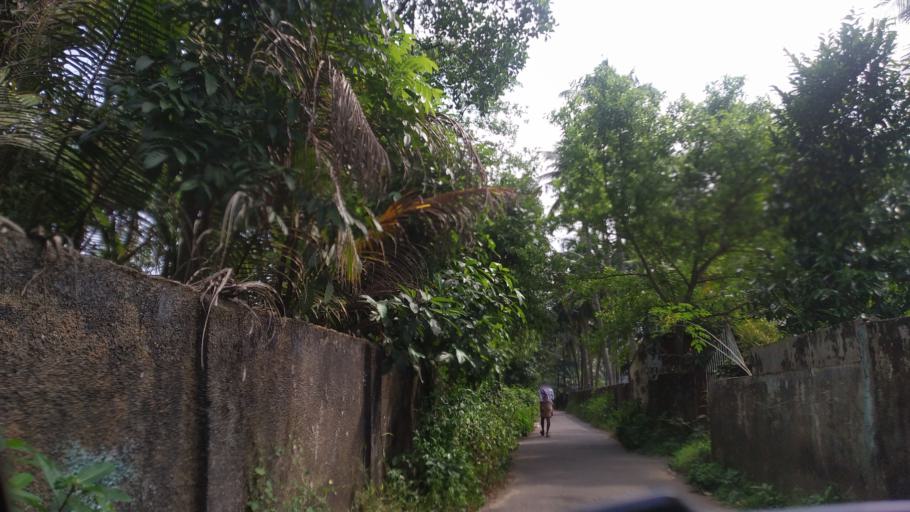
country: IN
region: Kerala
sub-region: Ernakulam
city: Elur
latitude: 10.0888
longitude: 76.2050
